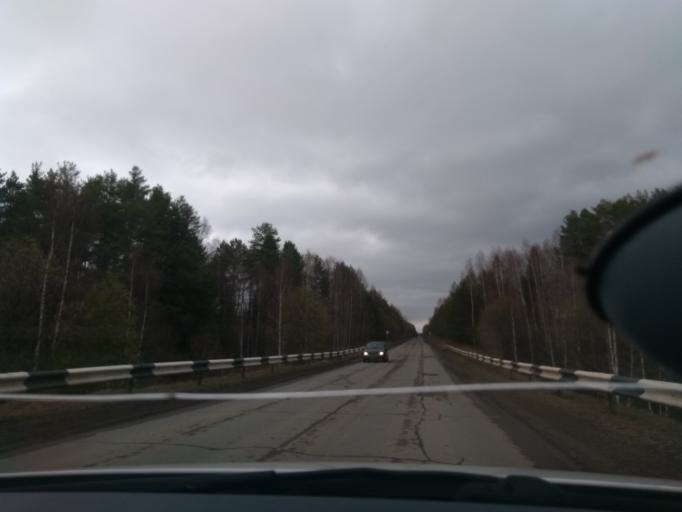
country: RU
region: Perm
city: Kungur
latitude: 57.3501
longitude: 56.7983
